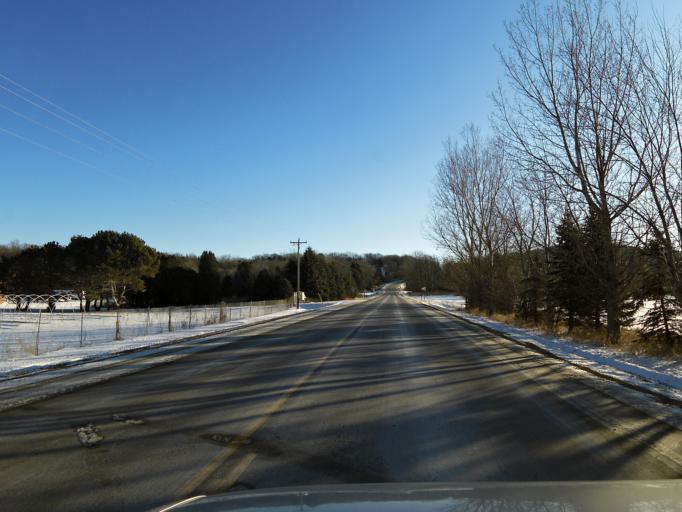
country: US
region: Minnesota
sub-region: Carver County
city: Carver
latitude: 44.7330
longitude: -93.5866
